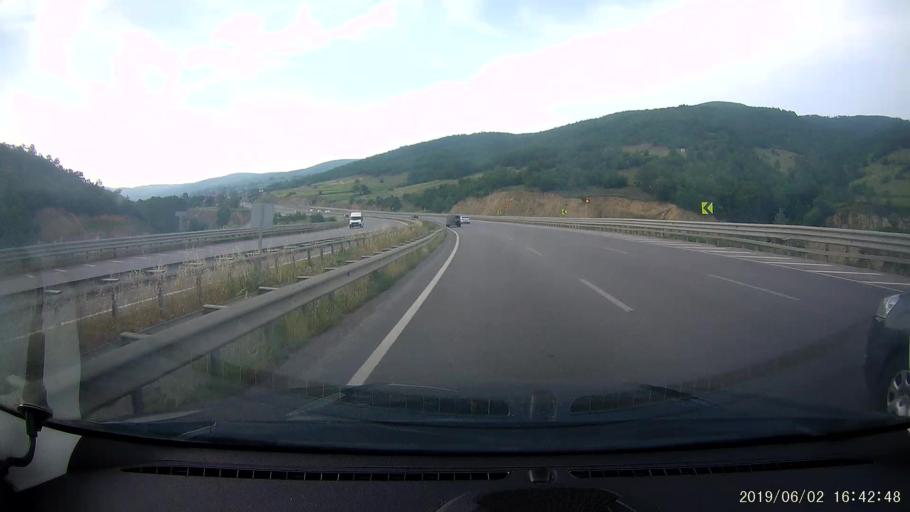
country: TR
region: Samsun
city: Kavak
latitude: 41.1239
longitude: 36.1379
